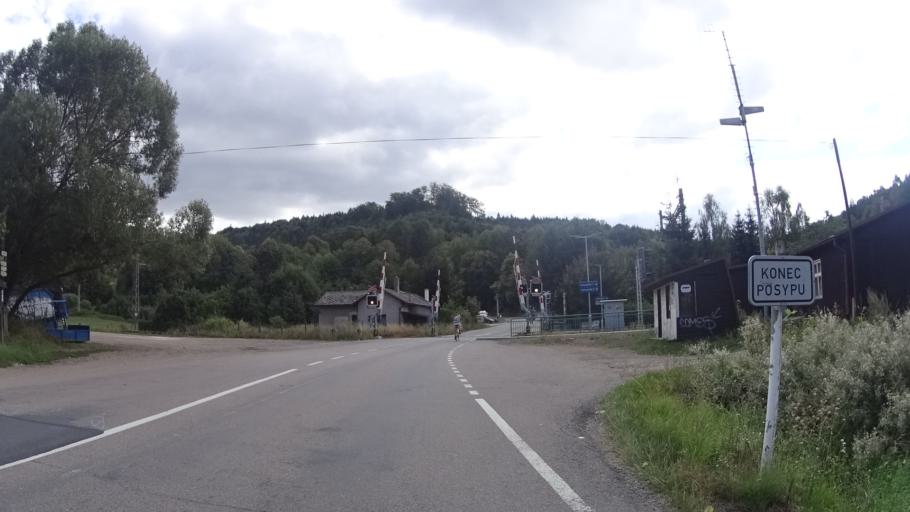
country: CZ
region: Pardubicky
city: Dolni Dobrouc
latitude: 49.9931
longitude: 16.4470
